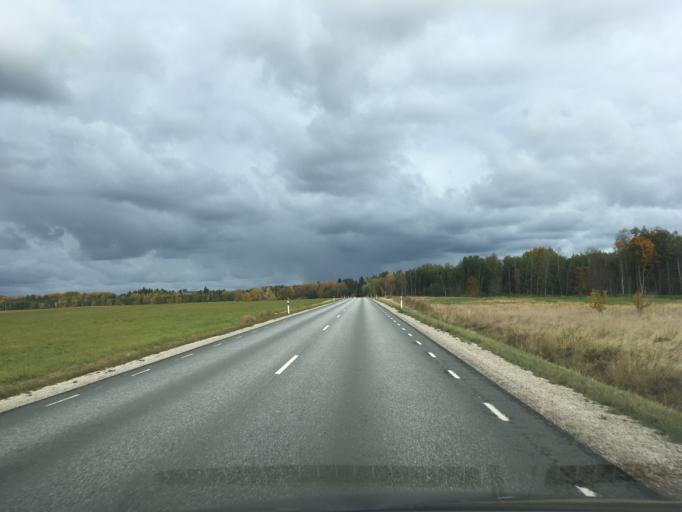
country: EE
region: Harju
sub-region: Anija vald
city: Kehra
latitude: 59.2852
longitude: 25.3746
